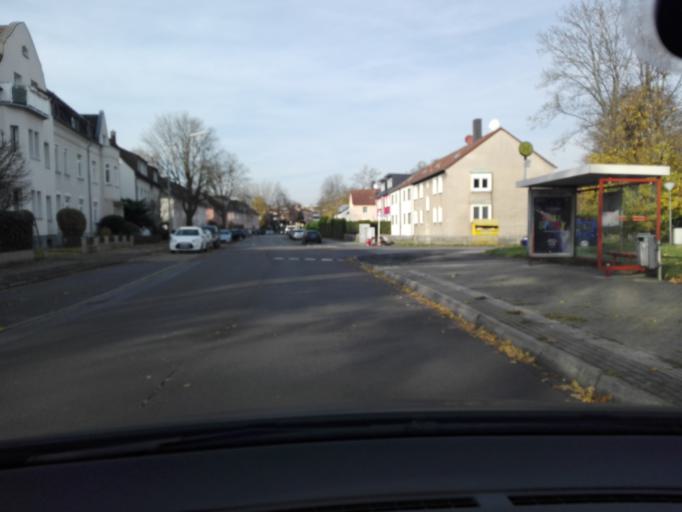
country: DE
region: North Rhine-Westphalia
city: Lanstrop
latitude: 51.5298
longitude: 7.5394
